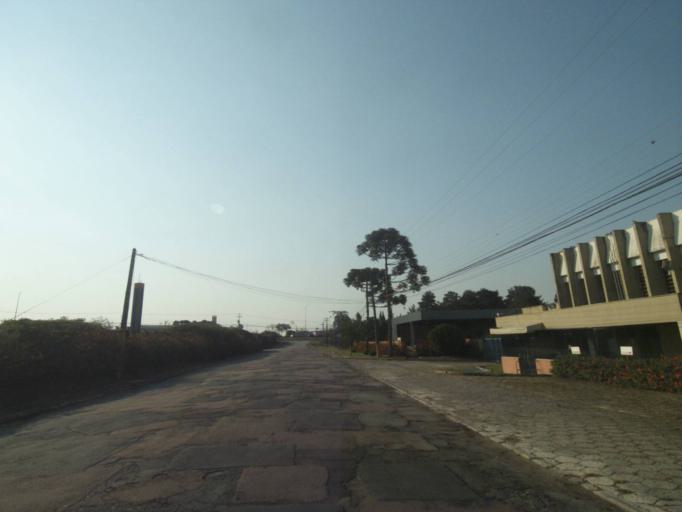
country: BR
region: Parana
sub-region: Curitiba
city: Curitiba
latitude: -25.4887
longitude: -49.2676
